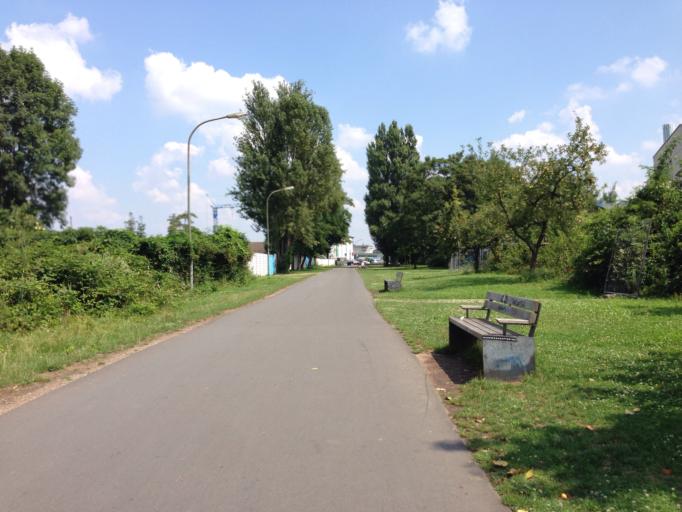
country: DE
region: Hesse
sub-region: Regierungsbezirk Darmstadt
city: Offenbach
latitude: 50.1106
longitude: 8.7368
